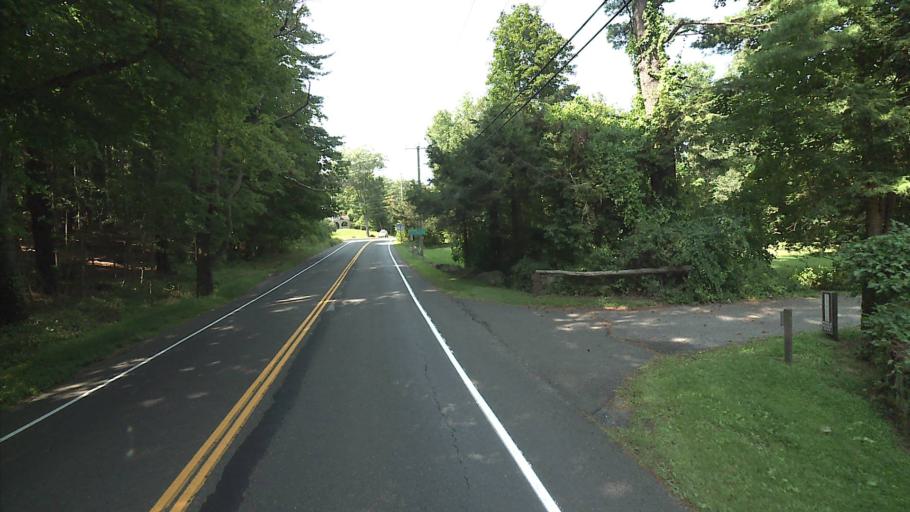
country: US
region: Connecticut
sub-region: Fairfield County
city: Bethel
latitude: 41.3378
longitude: -73.3797
